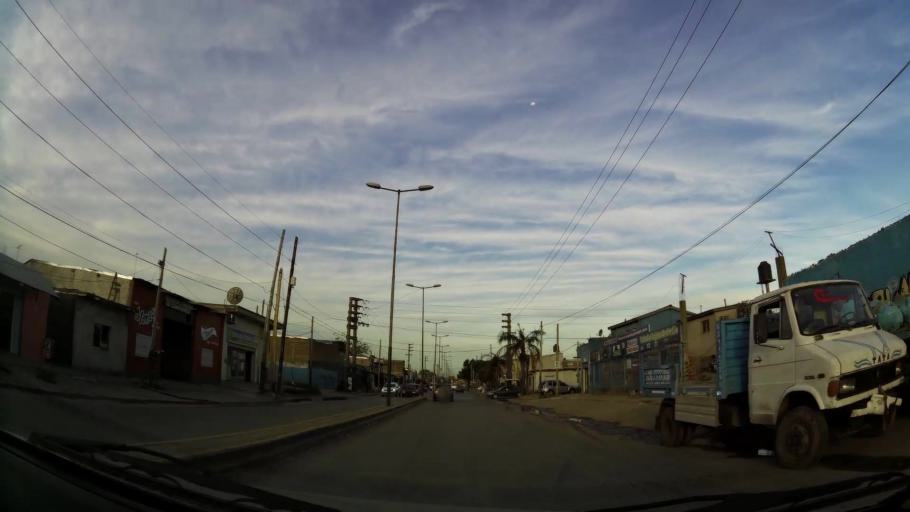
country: AR
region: Buenos Aires
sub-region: Partido de Almirante Brown
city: Adrogue
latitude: -34.7752
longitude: -58.3274
